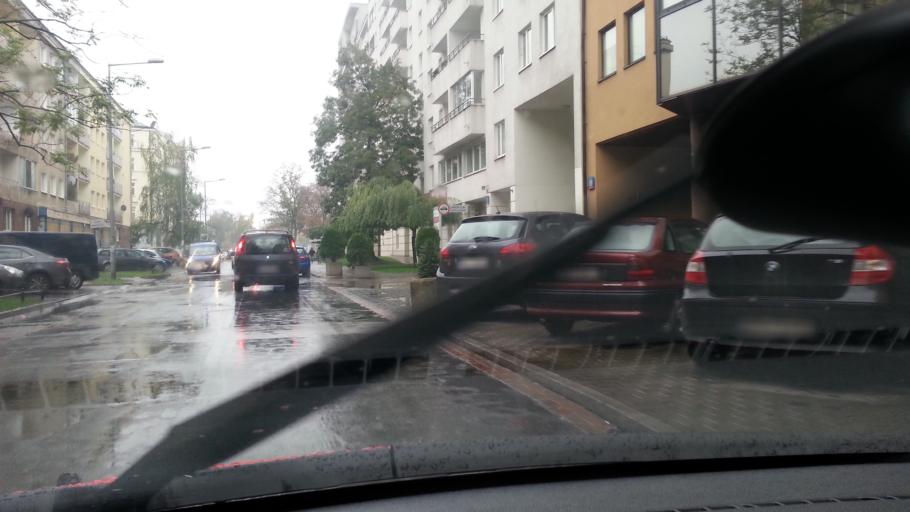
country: PL
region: Masovian Voivodeship
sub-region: Warszawa
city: Ochota
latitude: 52.2299
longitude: 20.9591
